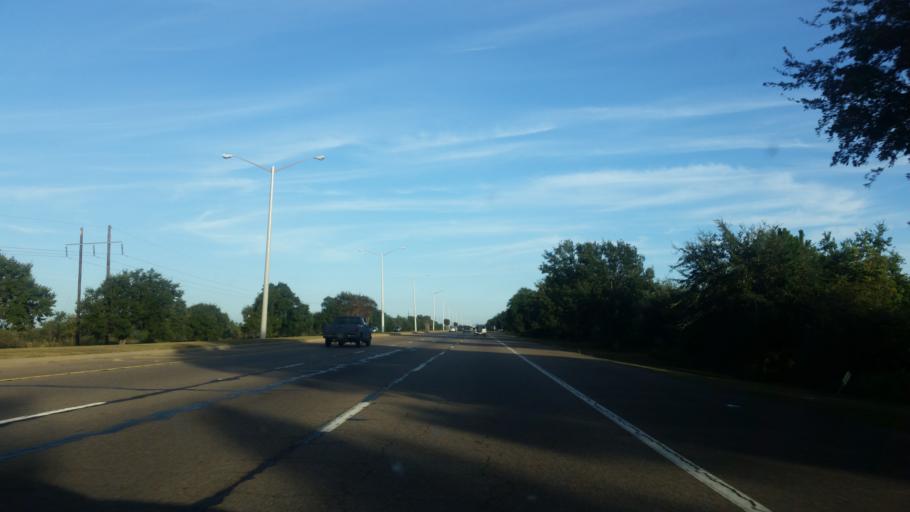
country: US
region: Mississippi
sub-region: Jackson County
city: Gautier
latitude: 30.3807
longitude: -88.5993
